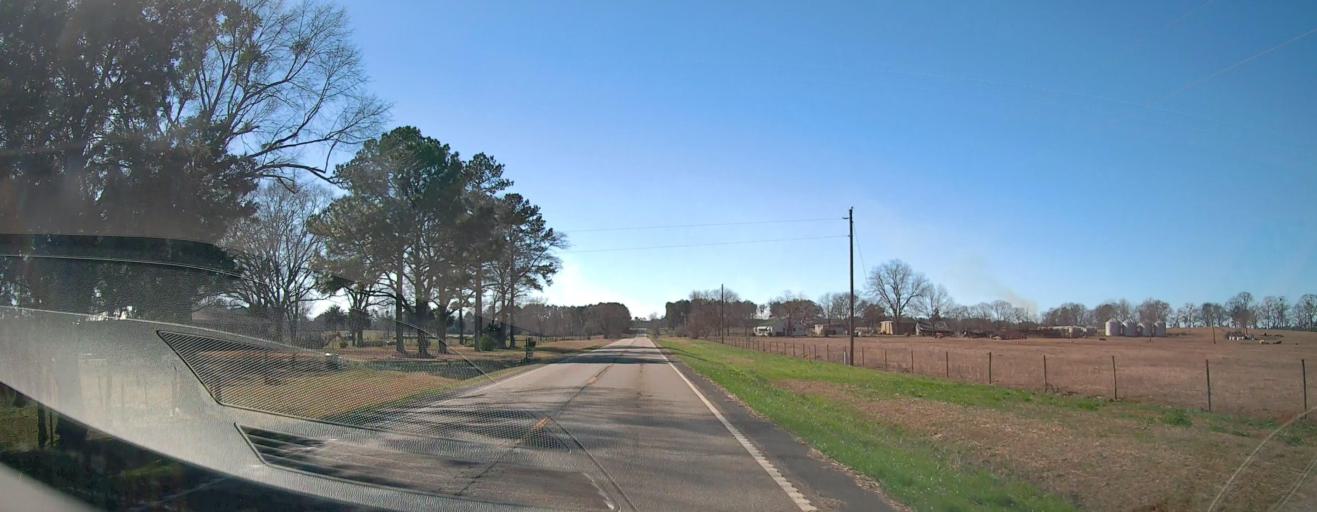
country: US
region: Georgia
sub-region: Sumter County
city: Americus
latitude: 32.1891
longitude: -84.1960
